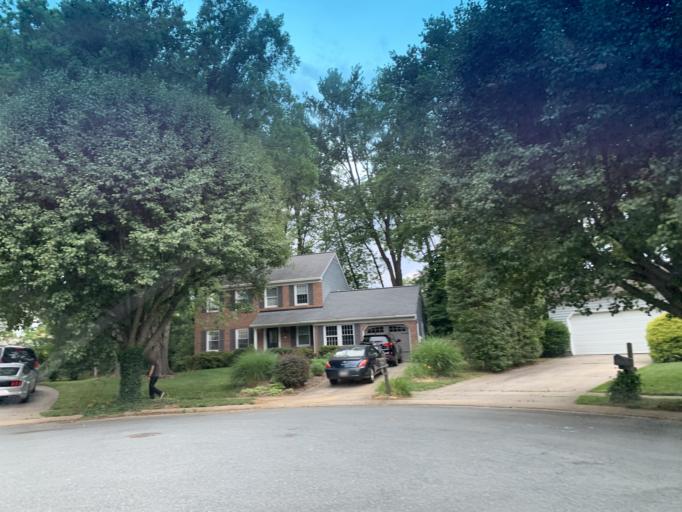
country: US
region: Maryland
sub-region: Harford County
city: Bel Air
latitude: 39.5204
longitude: -76.3540
